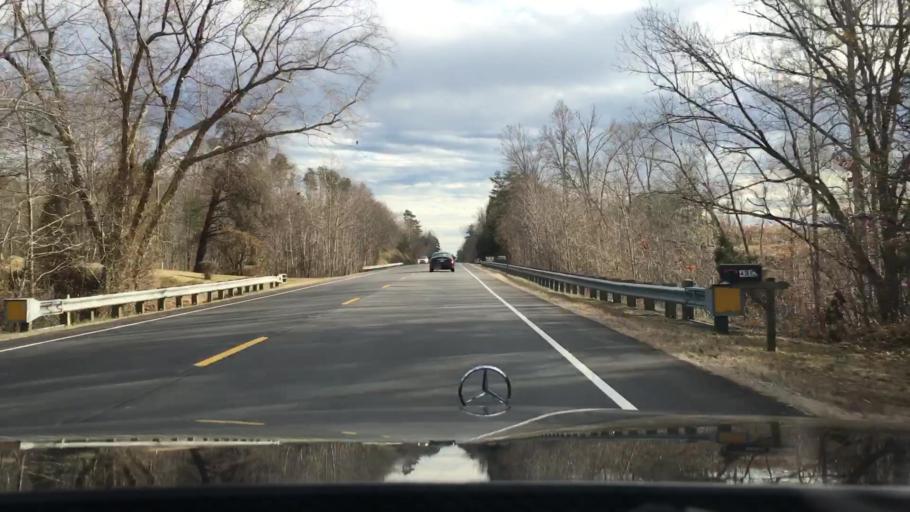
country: US
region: North Carolina
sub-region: Caswell County
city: Yanceyville
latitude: 36.4554
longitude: -79.3697
